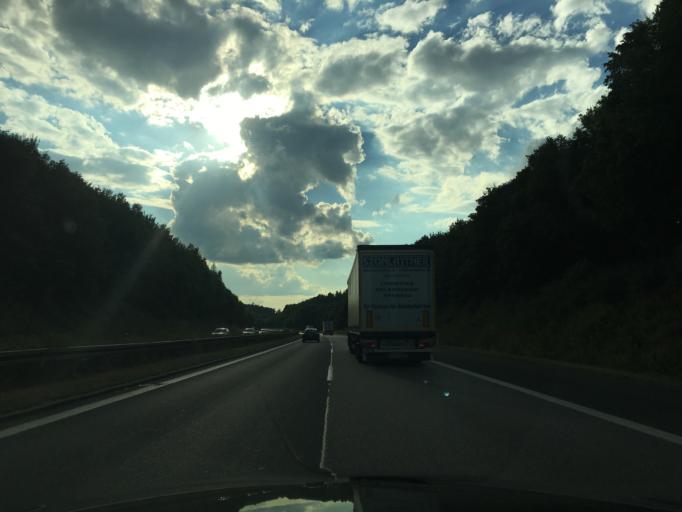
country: DE
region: Bavaria
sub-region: Regierungsbezirk Mittelfranken
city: Herrieden
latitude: 49.2634
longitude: 10.5331
